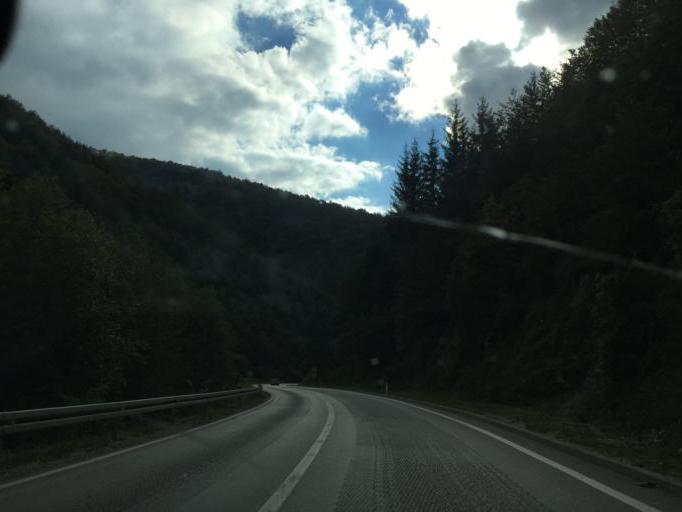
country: BA
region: Federation of Bosnia and Herzegovina
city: Novi Travnik
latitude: 44.0935
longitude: 17.5721
